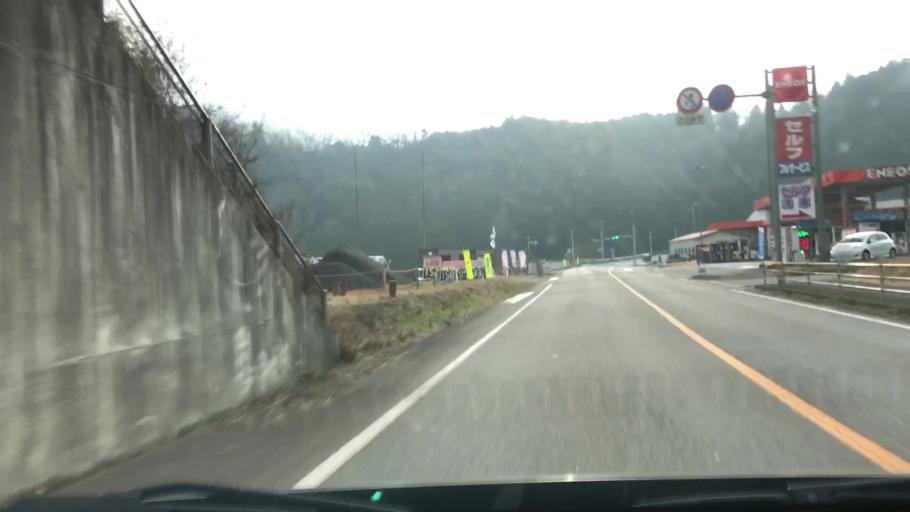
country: JP
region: Oita
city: Takedamachi
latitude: 32.9826
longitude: 131.5471
